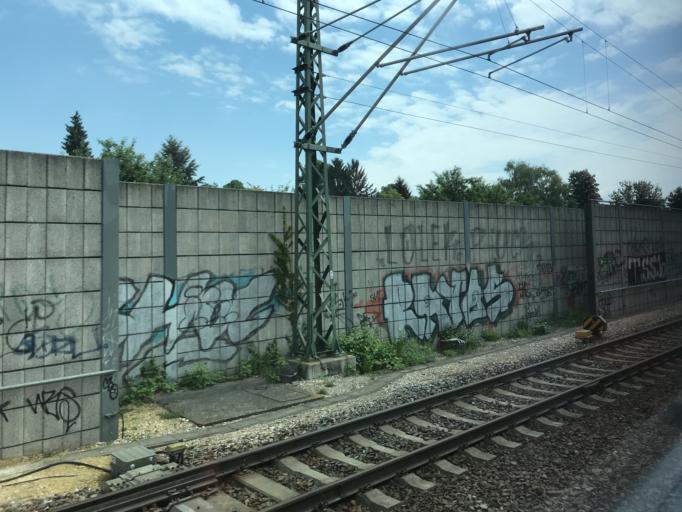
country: DE
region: Baden-Wuerttemberg
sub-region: Tuebingen Region
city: Ulm
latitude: 48.3945
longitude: 9.9857
